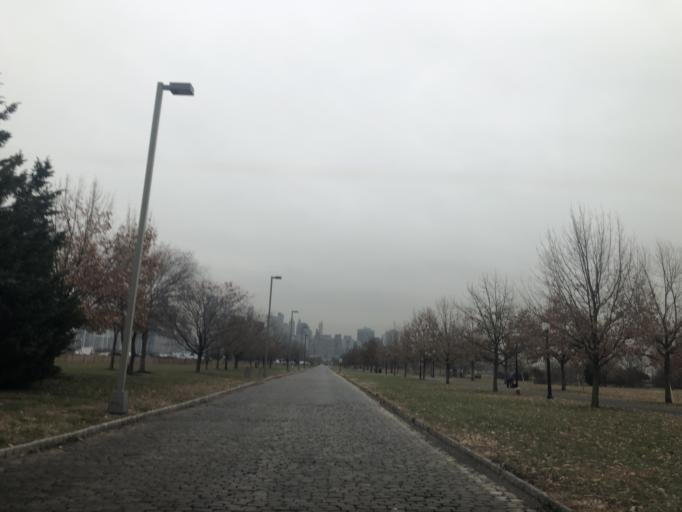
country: US
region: New Jersey
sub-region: Hudson County
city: Jersey City
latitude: 40.7095
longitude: -74.0473
